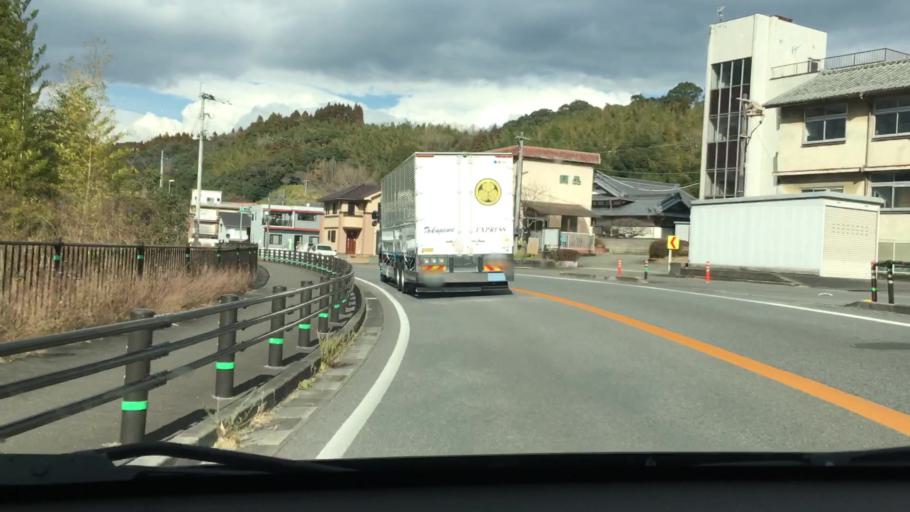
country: JP
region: Oita
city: Usuki
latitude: 33.0442
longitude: 131.6918
